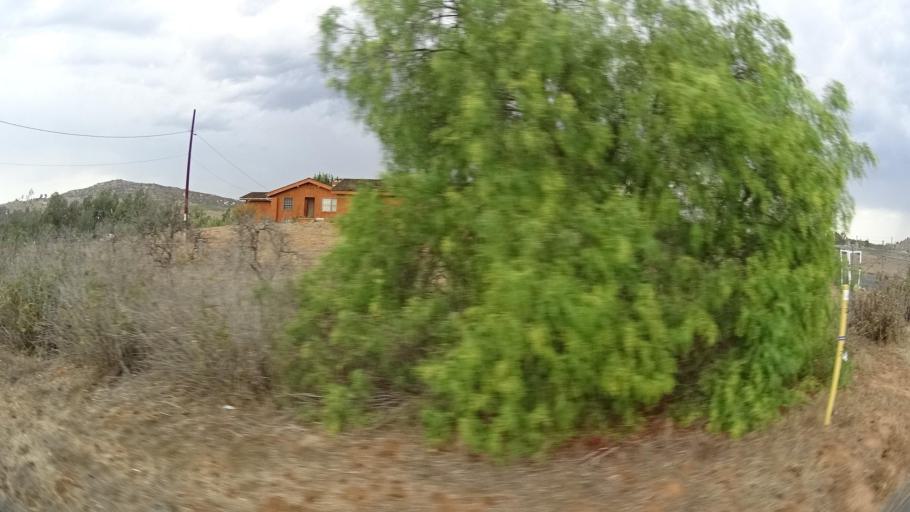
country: US
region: California
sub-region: San Diego County
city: San Pasqual
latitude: 33.0663
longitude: -117.0086
